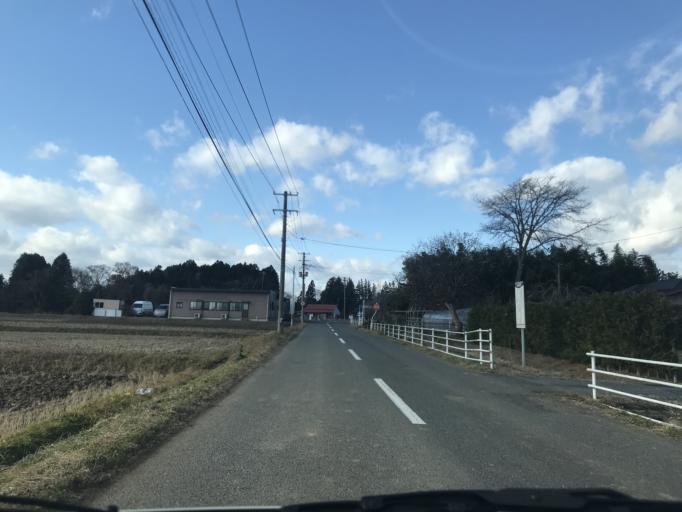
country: JP
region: Miyagi
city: Kogota
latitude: 38.7390
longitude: 141.0545
